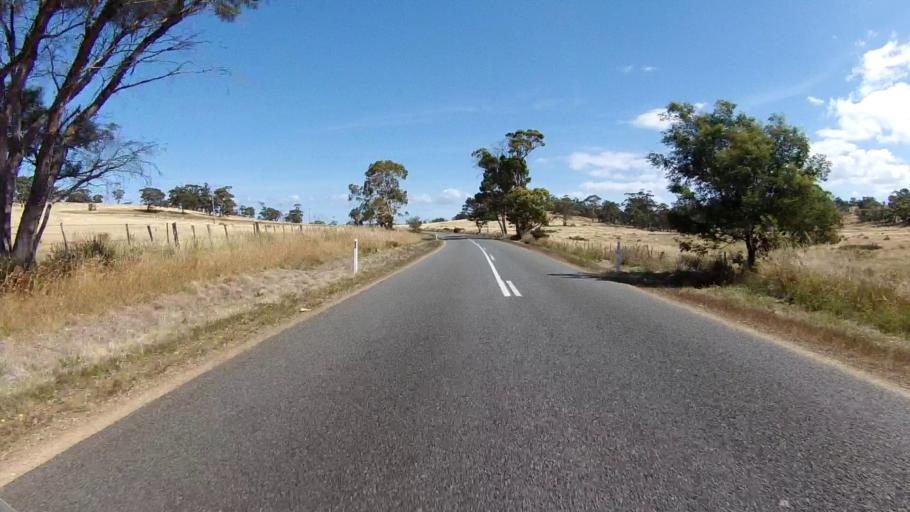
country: AU
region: Tasmania
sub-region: Sorell
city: Sorell
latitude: -42.2974
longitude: 147.9848
